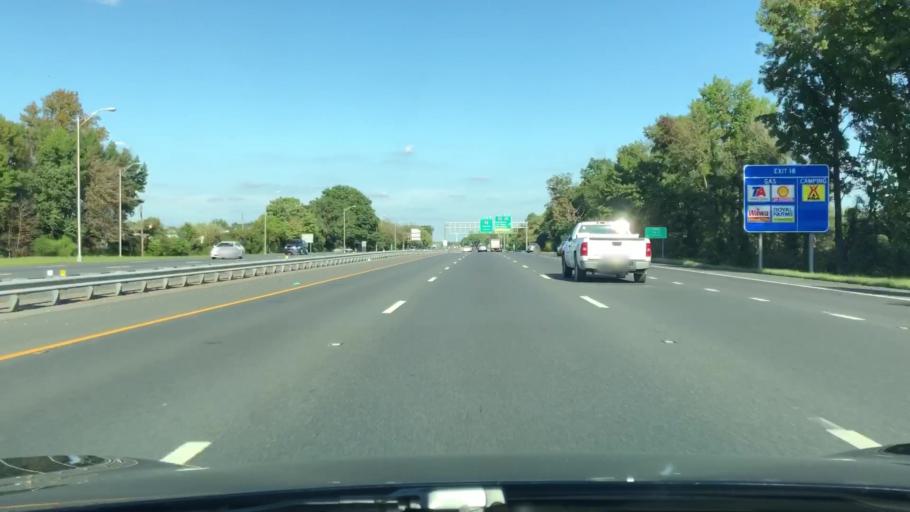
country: US
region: New Jersey
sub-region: Gloucester County
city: Paulsboro
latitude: 39.8160
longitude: -75.2545
